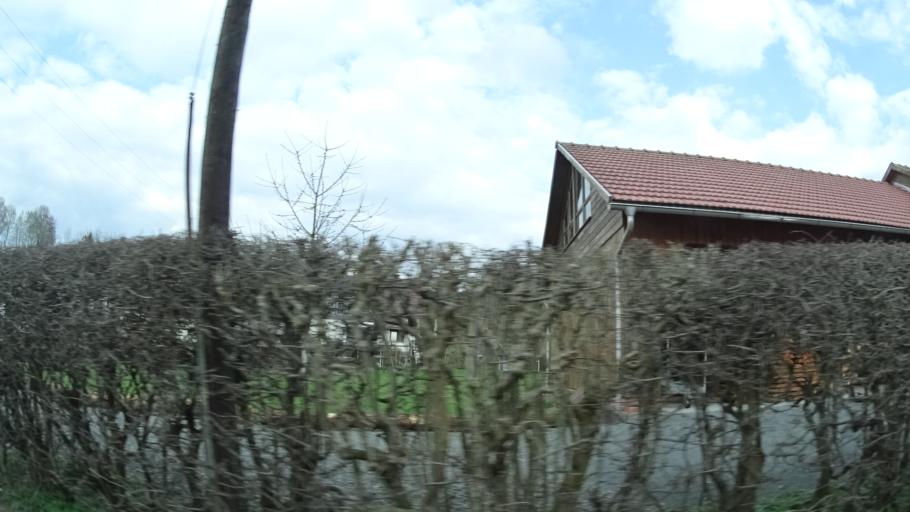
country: DE
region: Thuringia
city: Altersbach
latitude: 50.7426
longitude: 10.5089
